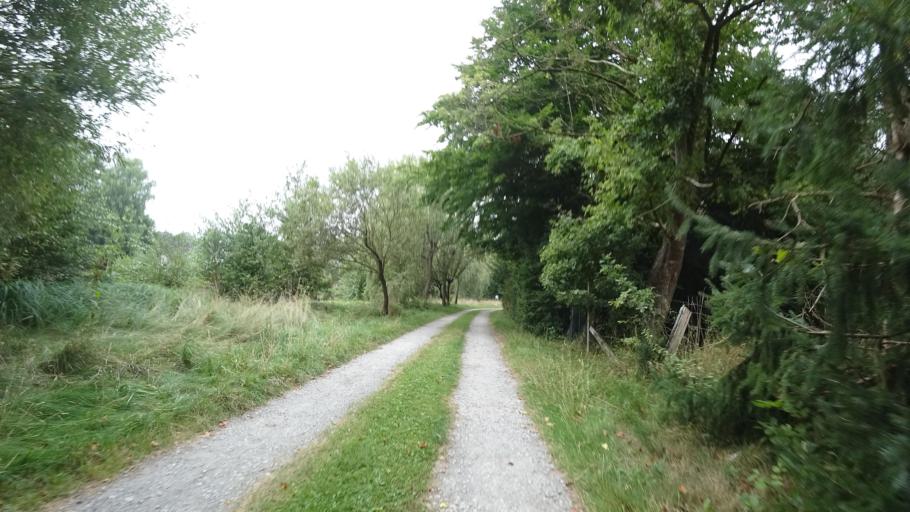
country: DE
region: North Rhine-Westphalia
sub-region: Regierungsbezirk Detmold
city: Guetersloh
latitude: 51.9042
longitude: 8.3278
